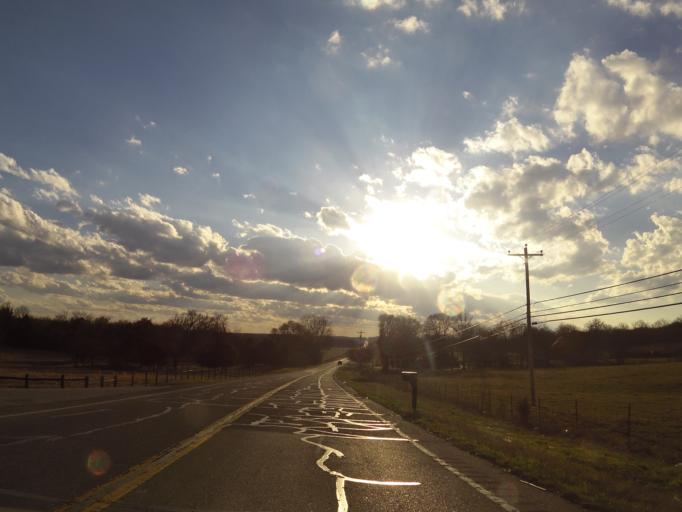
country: US
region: Tennessee
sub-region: Wilson County
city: Lebanon
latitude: 36.2261
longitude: -86.2216
